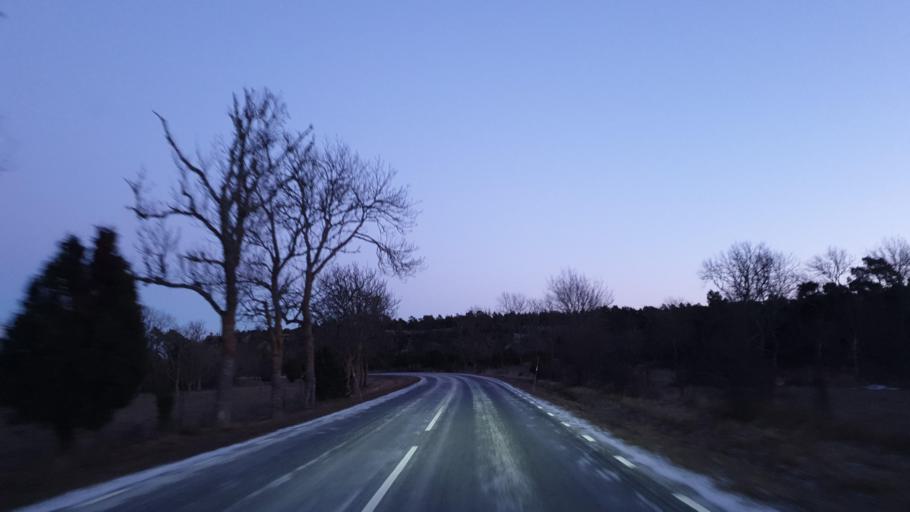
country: SE
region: Gotland
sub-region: Gotland
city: Slite
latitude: 57.4224
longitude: 18.8501
